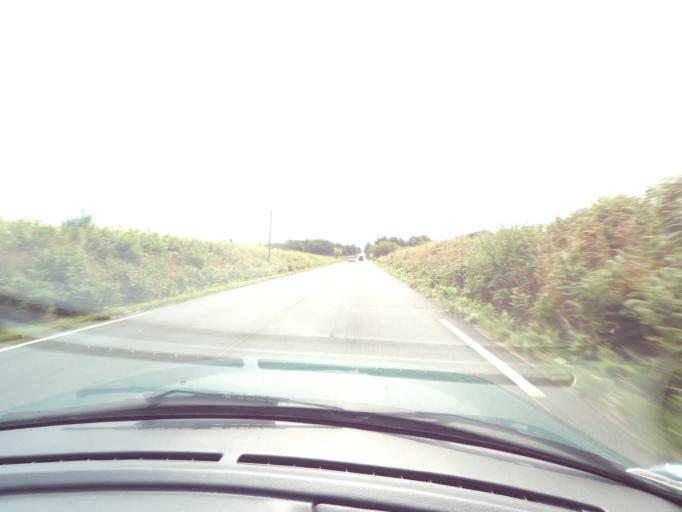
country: FR
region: Limousin
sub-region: Departement de la Haute-Vienne
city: Neuvic-Entier
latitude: 45.7470
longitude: 1.6013
